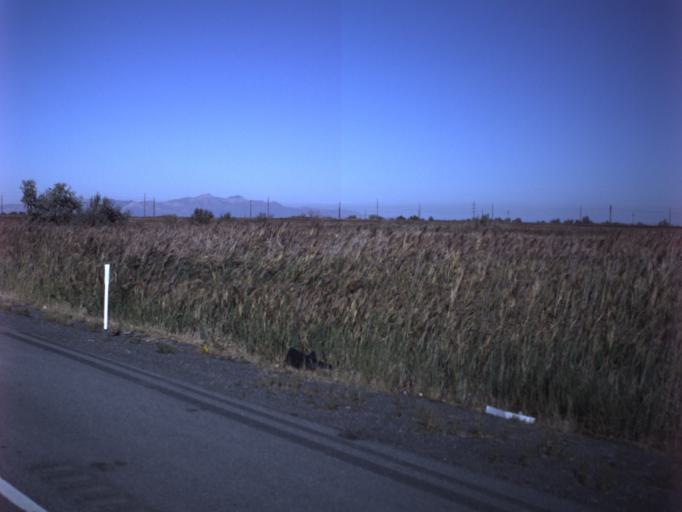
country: US
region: Utah
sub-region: Salt Lake County
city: Magna
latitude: 40.7278
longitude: -112.1815
